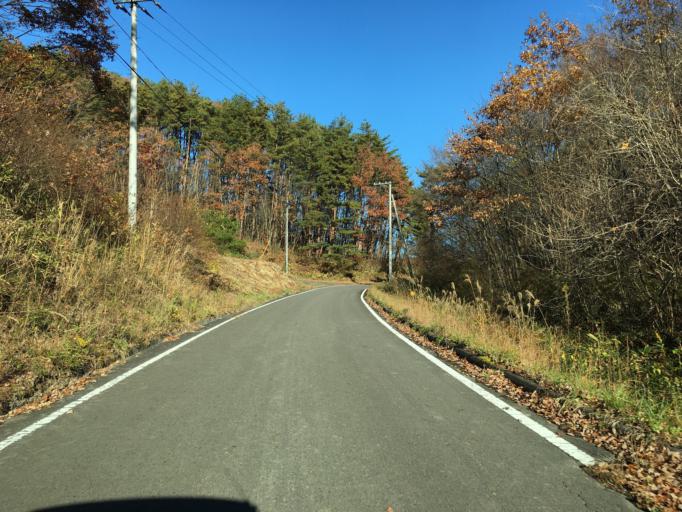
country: JP
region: Fukushima
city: Ishikawa
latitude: 37.2391
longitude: 140.5248
